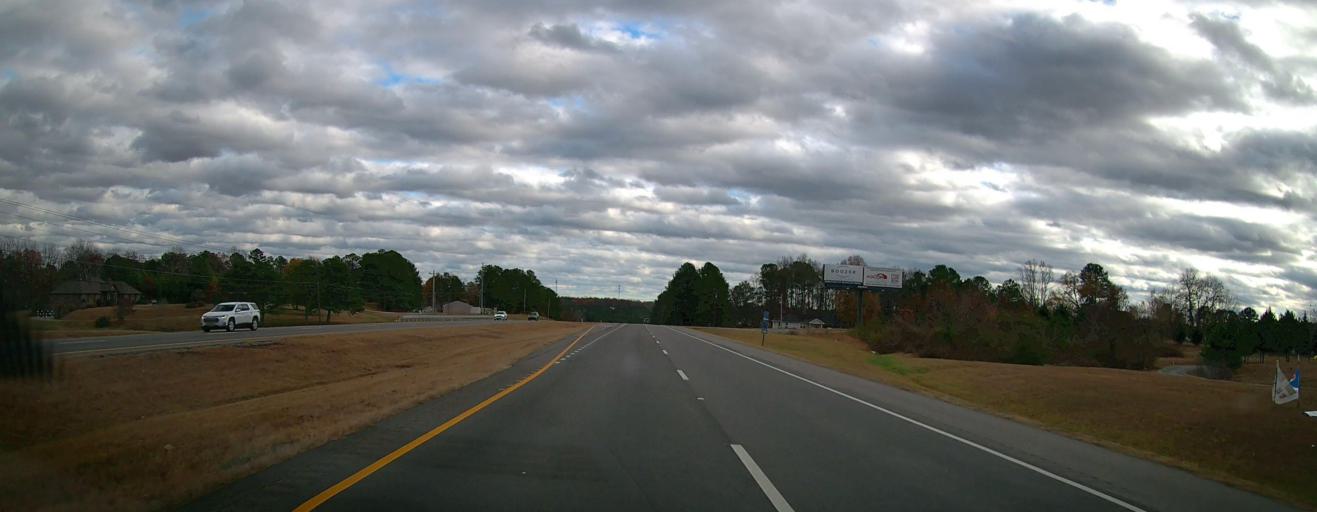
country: US
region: Alabama
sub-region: Cullman County
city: Cullman
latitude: 34.2166
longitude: -86.8940
